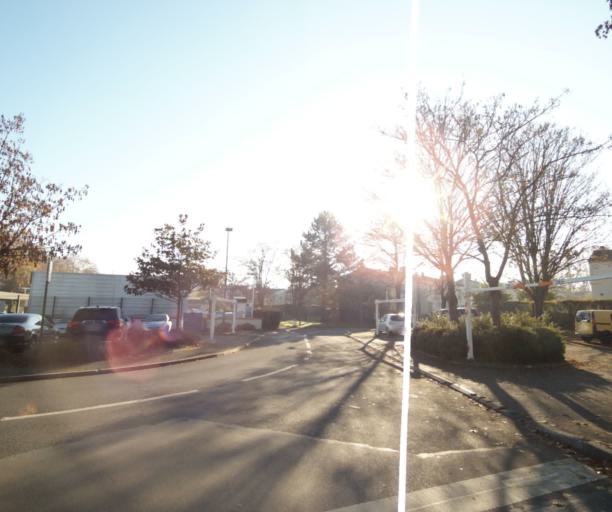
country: FR
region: Ile-de-France
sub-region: Departement du Val-d'Oise
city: Arnouville
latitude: 48.9924
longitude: 2.4274
